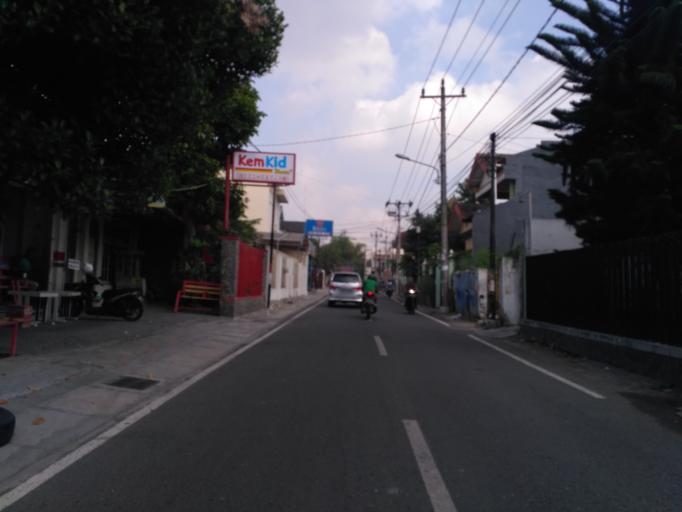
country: ID
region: Daerah Istimewa Yogyakarta
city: Yogyakarta
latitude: -7.7932
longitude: 110.3581
